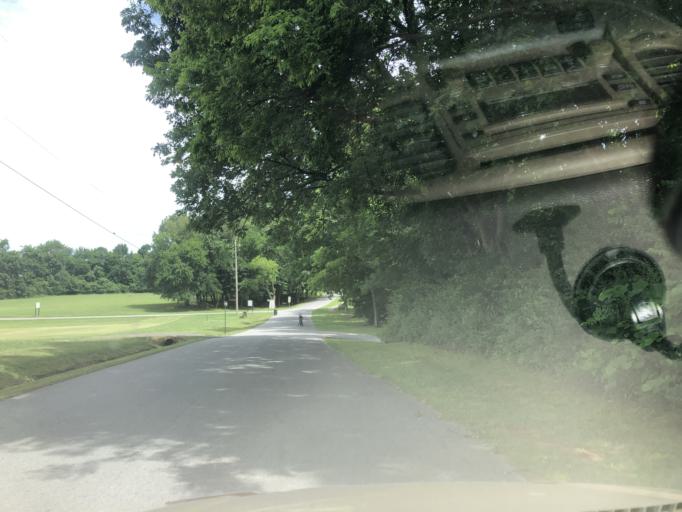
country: US
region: Tennessee
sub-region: Davidson County
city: Lakewood
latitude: 36.2523
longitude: -86.6035
